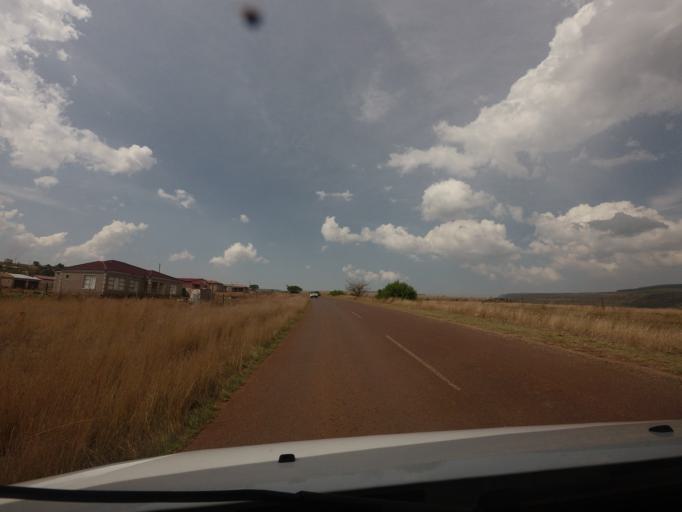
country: ZA
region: Mpumalanga
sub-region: Ehlanzeni District
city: Graksop
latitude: -24.6638
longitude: 30.8139
